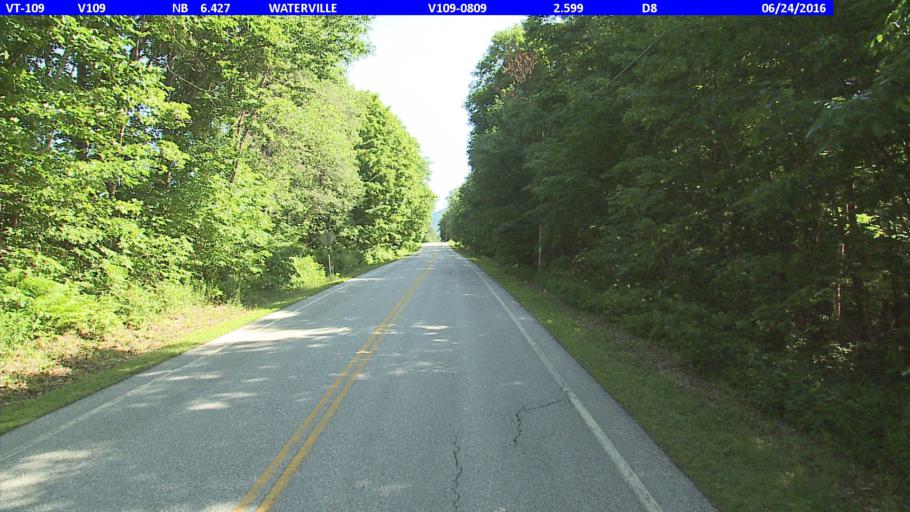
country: US
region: Vermont
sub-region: Lamoille County
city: Johnson
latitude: 44.7156
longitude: -72.7535
